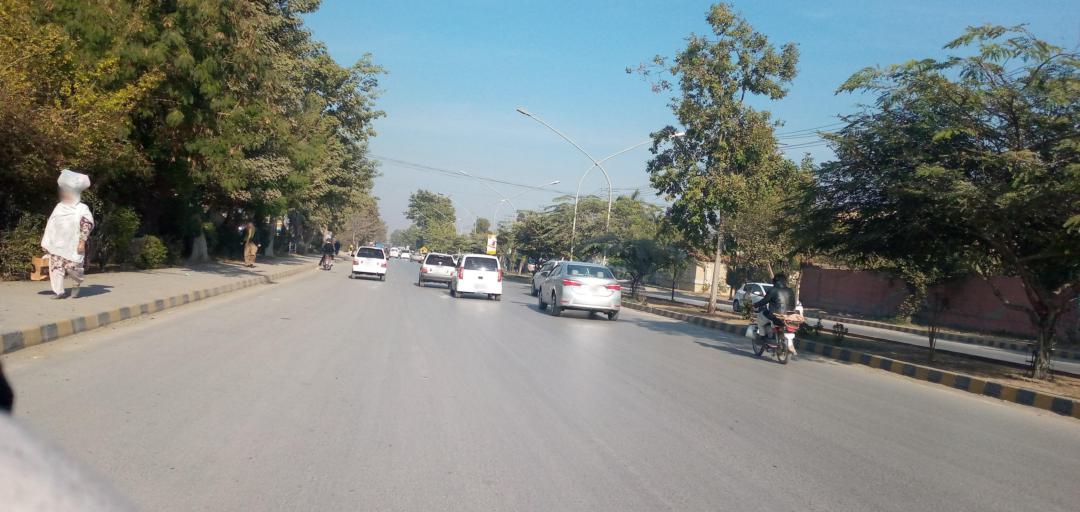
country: PK
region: Khyber Pakhtunkhwa
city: Peshawar
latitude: 33.9711
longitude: 71.4420
